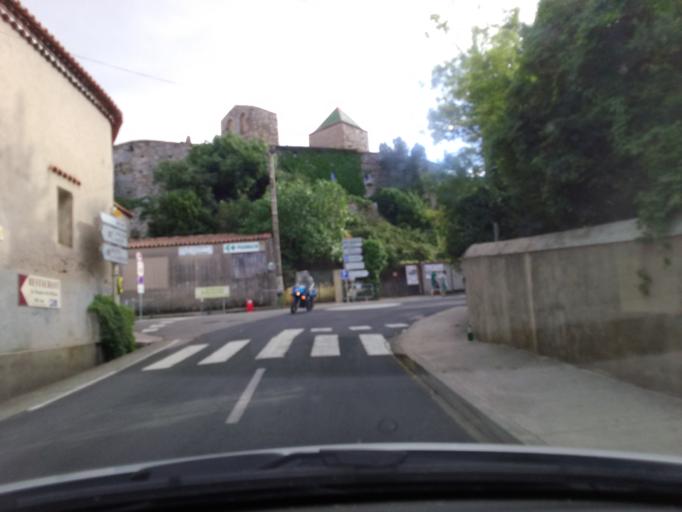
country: FR
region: Languedoc-Roussillon
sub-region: Departement de l'Herault
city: Saint-Jean-de-Fos
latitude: 43.7026
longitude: 3.5528
